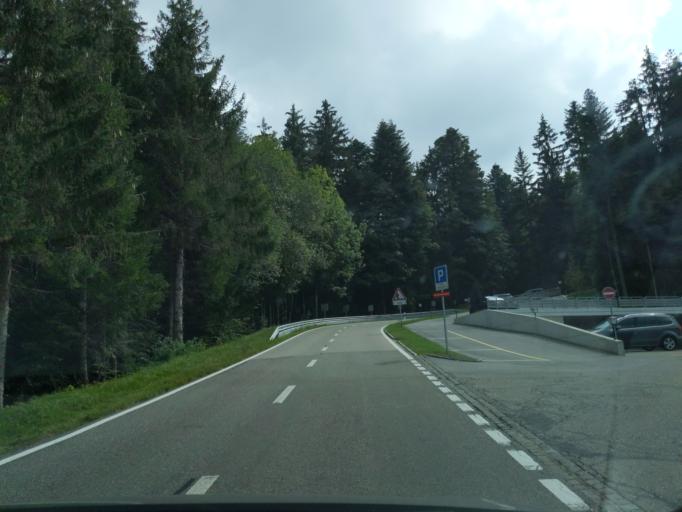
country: CH
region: Bern
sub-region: Oberaargau
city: Wyssachen
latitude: 47.0599
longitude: 7.8382
